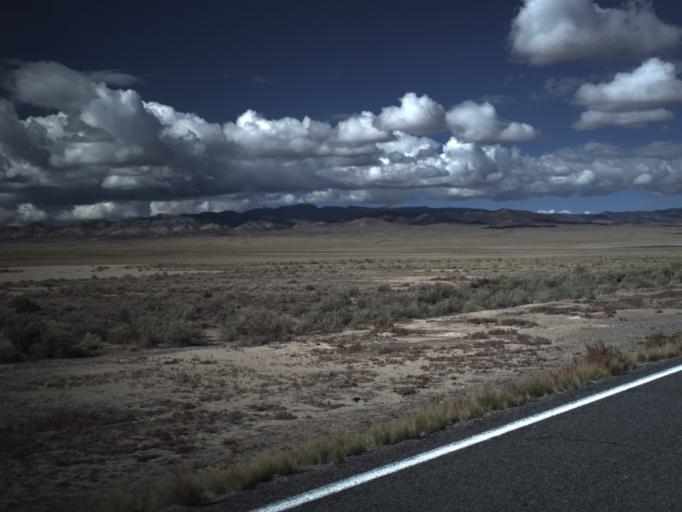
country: US
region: Utah
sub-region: Beaver County
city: Milford
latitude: 38.5420
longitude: -113.7081
